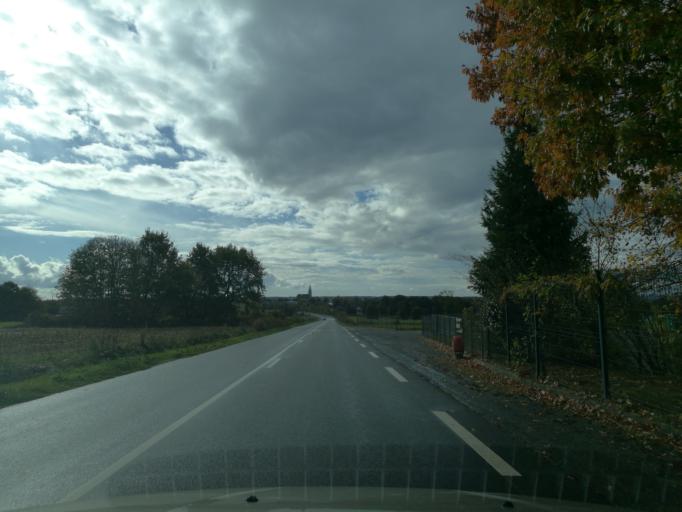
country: FR
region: Brittany
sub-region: Departement d'Ille-et-Vilaine
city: Bedee
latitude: 48.1953
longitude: -1.9407
